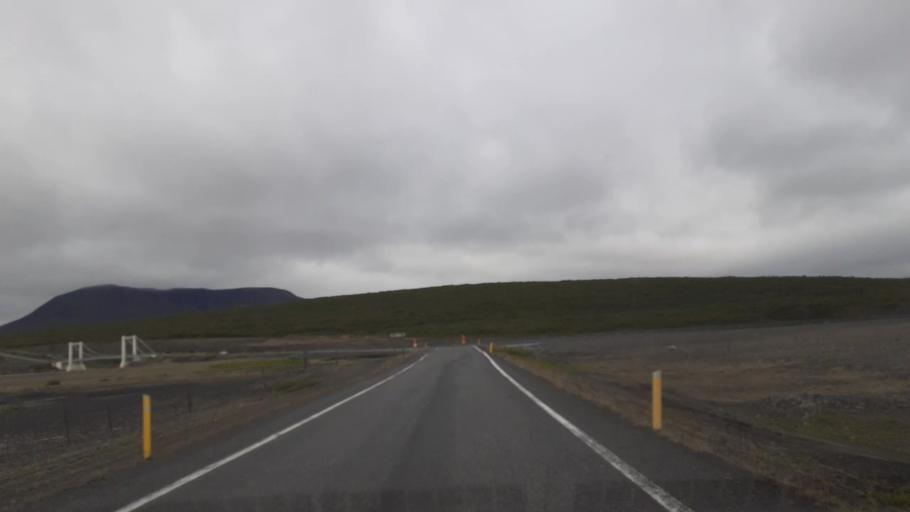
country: IS
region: Northeast
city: Husavik
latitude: 66.0309
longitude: -16.4526
